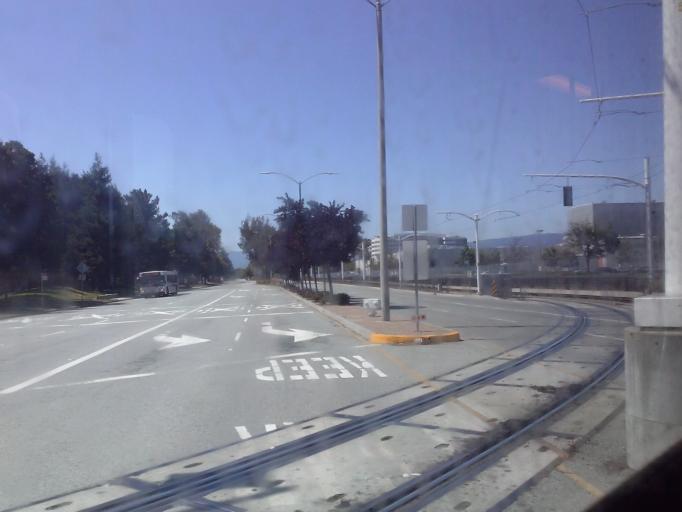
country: US
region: California
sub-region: Santa Clara County
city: Sunnyvale
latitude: 37.4141
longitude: -122.0253
